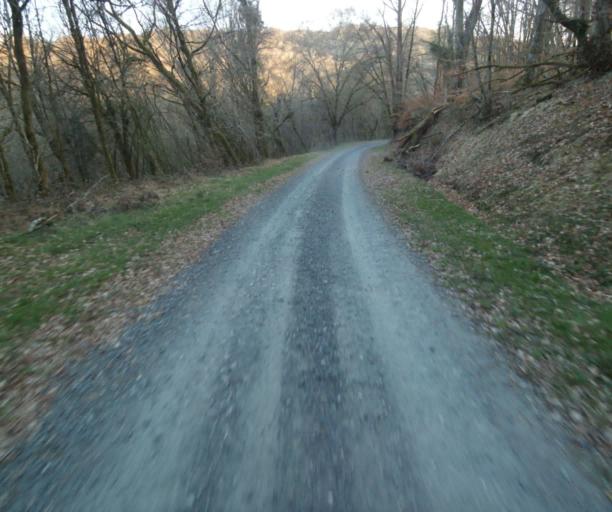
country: FR
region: Limousin
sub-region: Departement de la Correze
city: Uzerche
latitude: 45.3538
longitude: 1.6015
